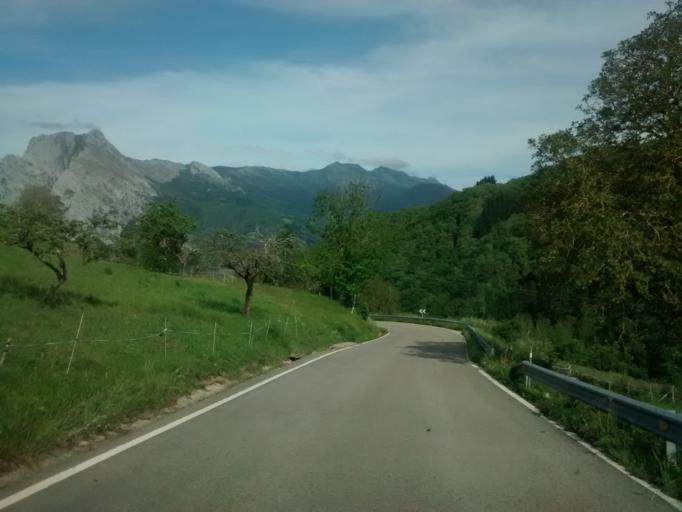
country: ES
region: Cantabria
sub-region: Provincia de Cantabria
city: Potes
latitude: 43.1909
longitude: -4.6347
